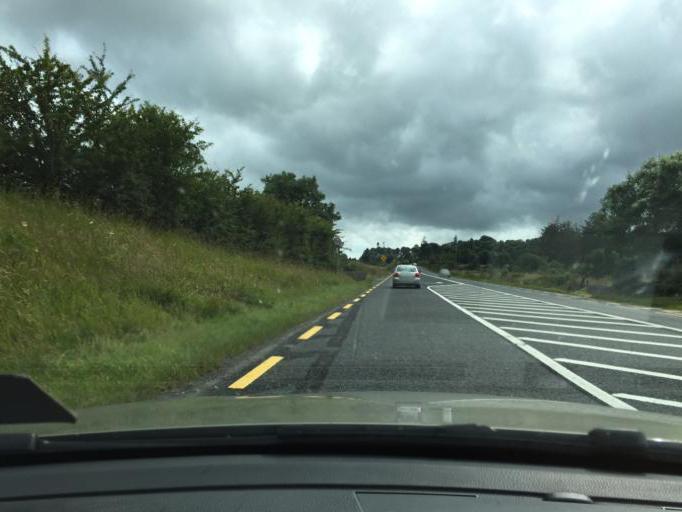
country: IE
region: Munster
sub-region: Waterford
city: Dungarvan
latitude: 52.1543
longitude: -7.5345
